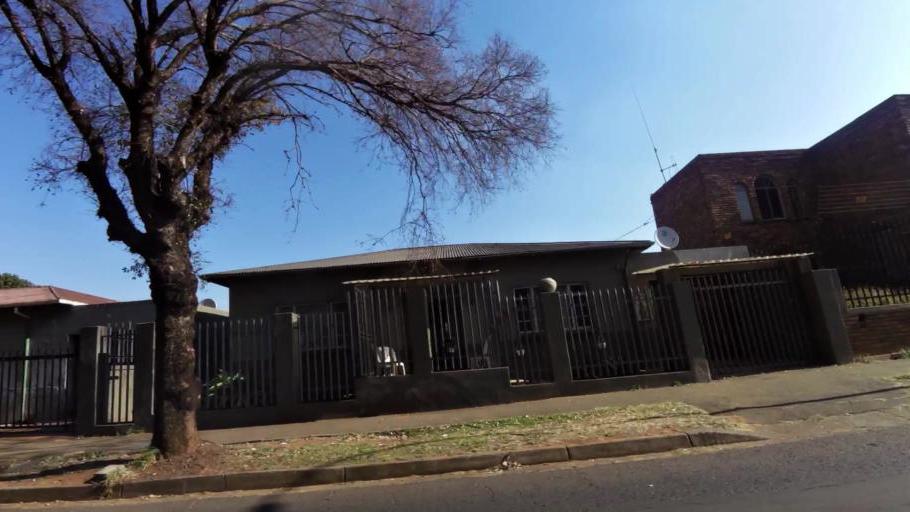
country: ZA
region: Gauteng
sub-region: City of Johannesburg Metropolitan Municipality
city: Johannesburg
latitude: -26.1719
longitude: 27.9683
